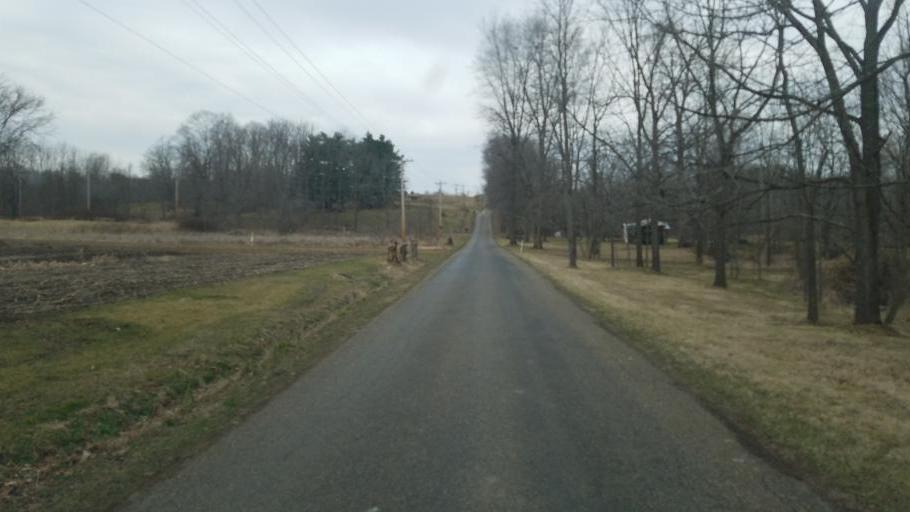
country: US
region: Ohio
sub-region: Ashland County
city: Loudonville
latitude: 40.7046
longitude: -82.2887
